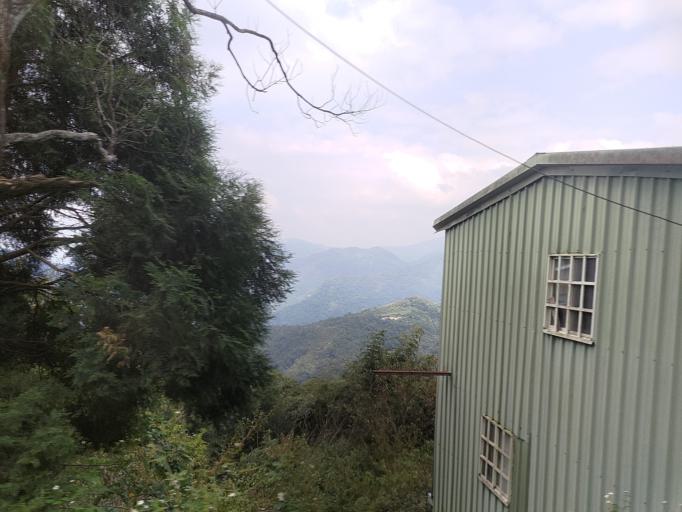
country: TW
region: Taiwan
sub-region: Hsinchu
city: Hsinchu
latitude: 24.6115
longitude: 121.0981
